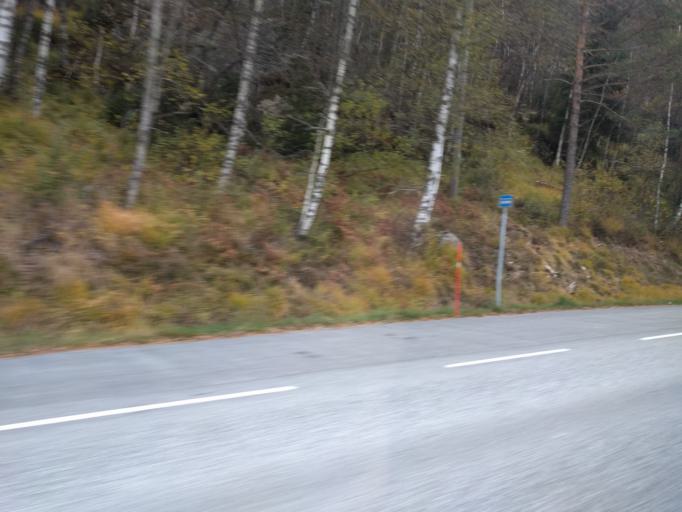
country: NO
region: Aust-Agder
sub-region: Iveland
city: Birketveit
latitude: 58.3756
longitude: 7.7617
